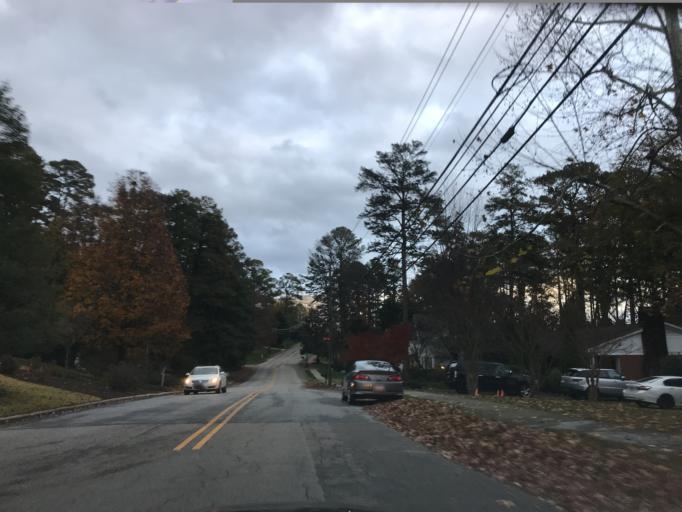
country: US
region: North Carolina
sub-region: Wake County
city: West Raleigh
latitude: 35.8367
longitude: -78.6484
